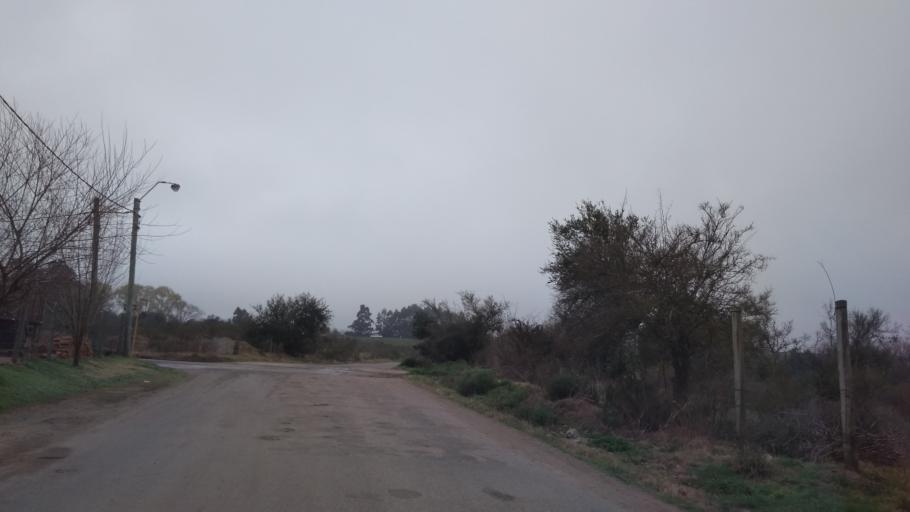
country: UY
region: Florida
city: Florida
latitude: -34.0905
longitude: -56.2091
